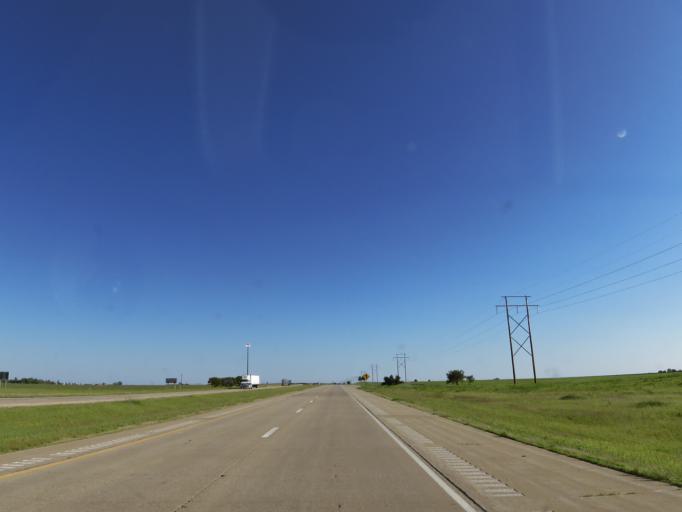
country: US
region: Illinois
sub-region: Woodford County
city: Minonk
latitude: 40.9104
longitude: -89.0569
